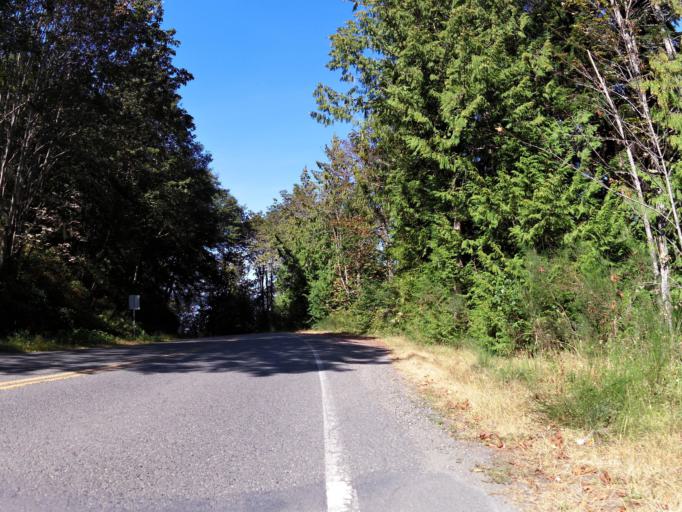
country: CA
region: British Columbia
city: North Saanich
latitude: 48.6182
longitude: -123.5224
